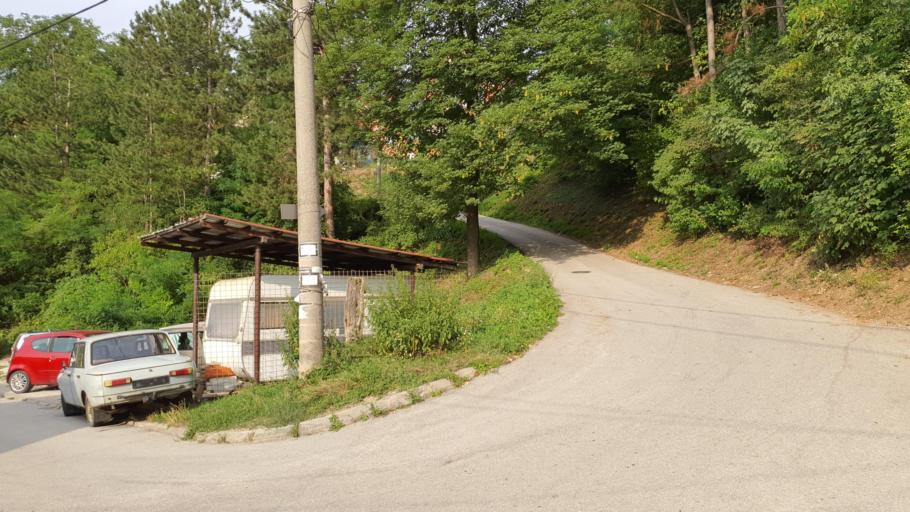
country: RS
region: Central Serbia
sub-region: Zlatiborski Okrug
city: Uzice
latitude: 43.8559
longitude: 19.8254
